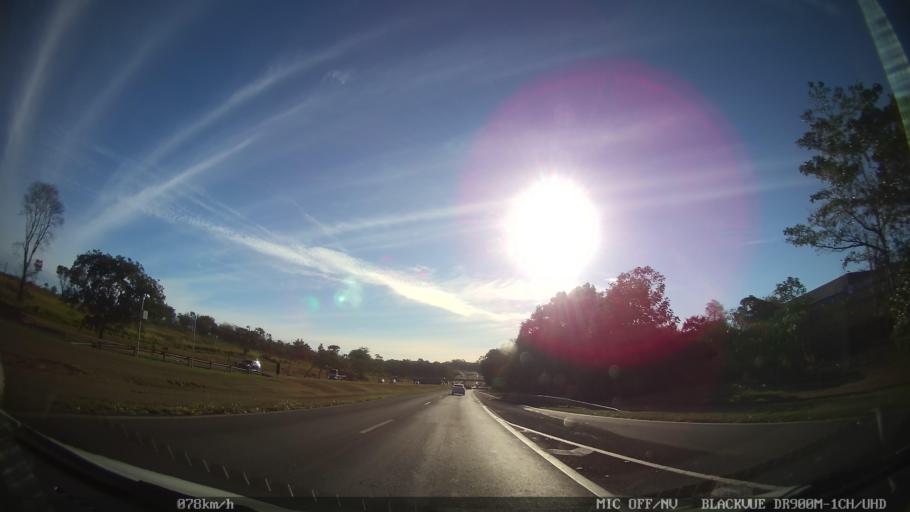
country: BR
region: Sao Paulo
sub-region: Sao Jose Do Rio Preto
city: Sao Jose do Rio Preto
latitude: -20.8205
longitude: -49.4298
